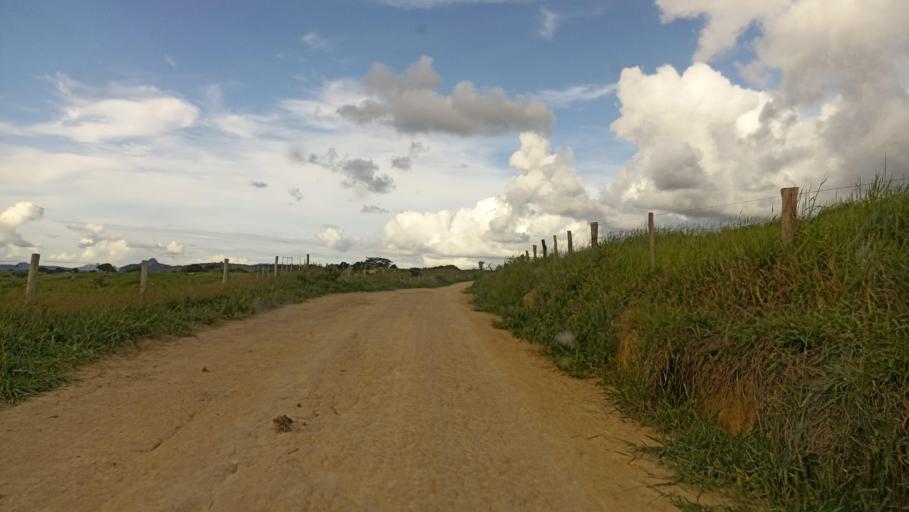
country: BR
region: Minas Gerais
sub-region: Almenara
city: Almenara
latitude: -16.5473
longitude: -40.4505
